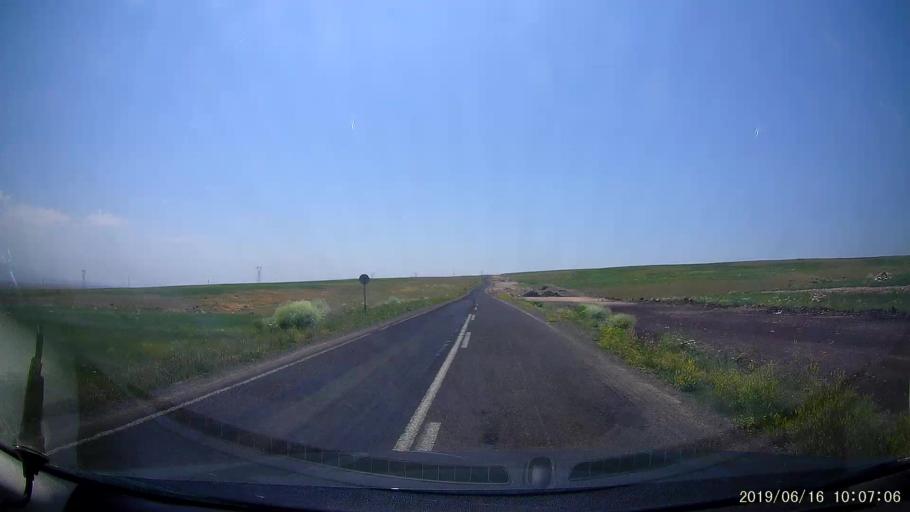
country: TR
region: Kars
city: Digor
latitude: 40.2478
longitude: 43.5512
